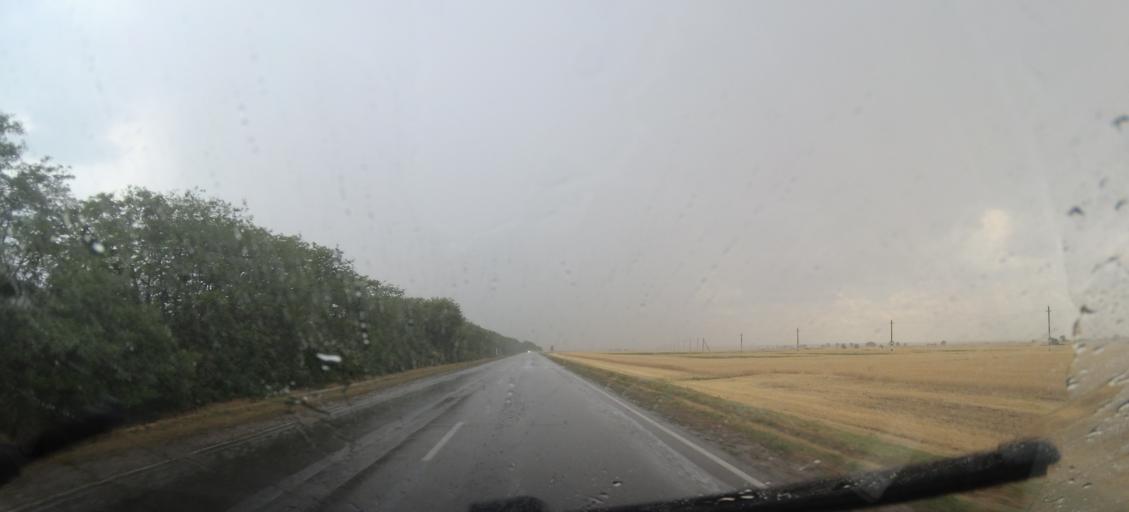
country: RU
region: Rostov
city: Proletarsk
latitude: 46.6670
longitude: 41.6902
